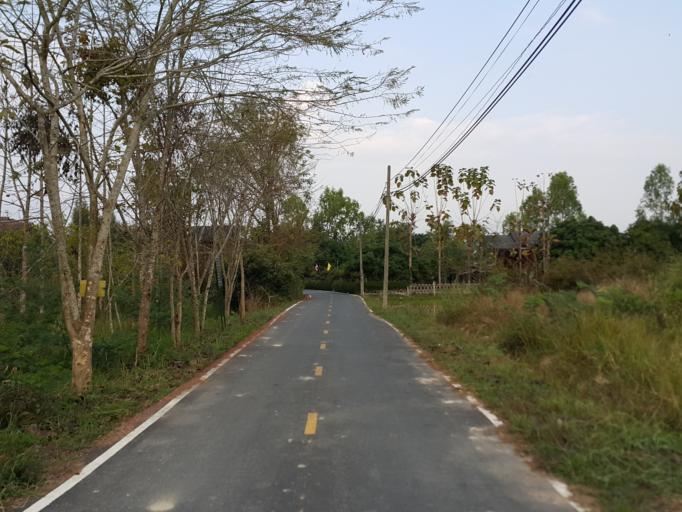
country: TH
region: Chiang Mai
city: San Sai
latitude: 18.8195
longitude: 99.0791
